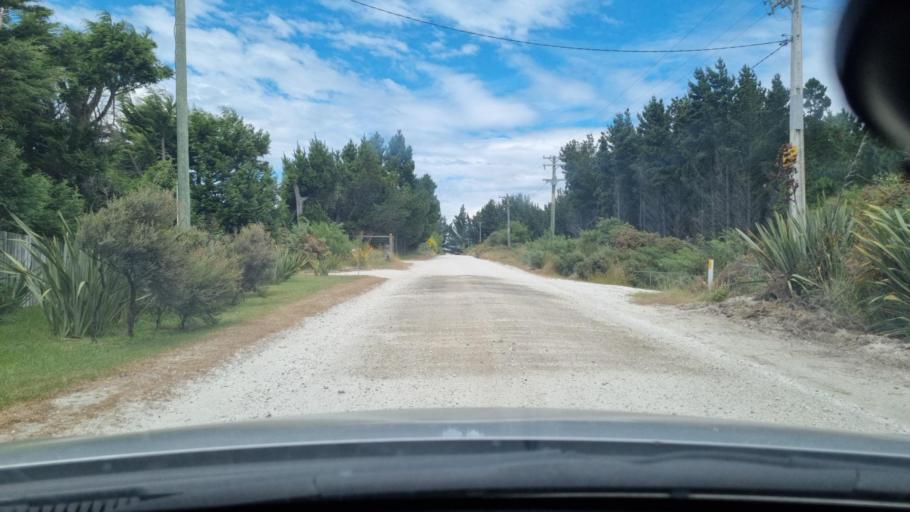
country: NZ
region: Southland
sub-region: Invercargill City
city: Bluff
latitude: -46.5576
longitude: 168.4335
